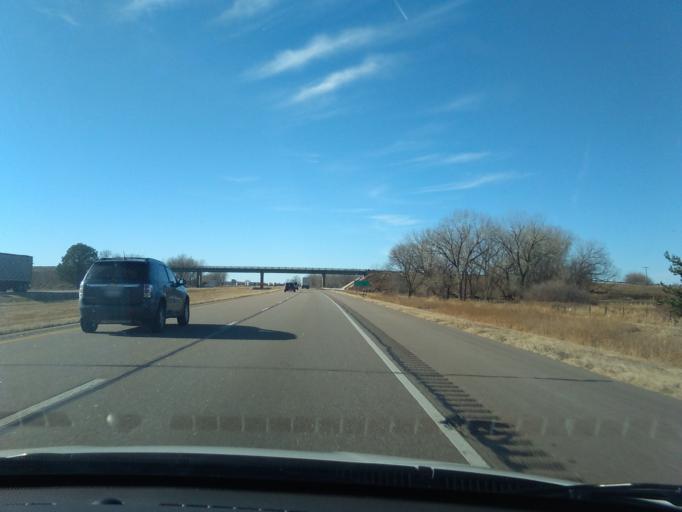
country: US
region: Nebraska
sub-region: Hall County
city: Wood River
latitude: 40.7575
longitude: -98.6047
